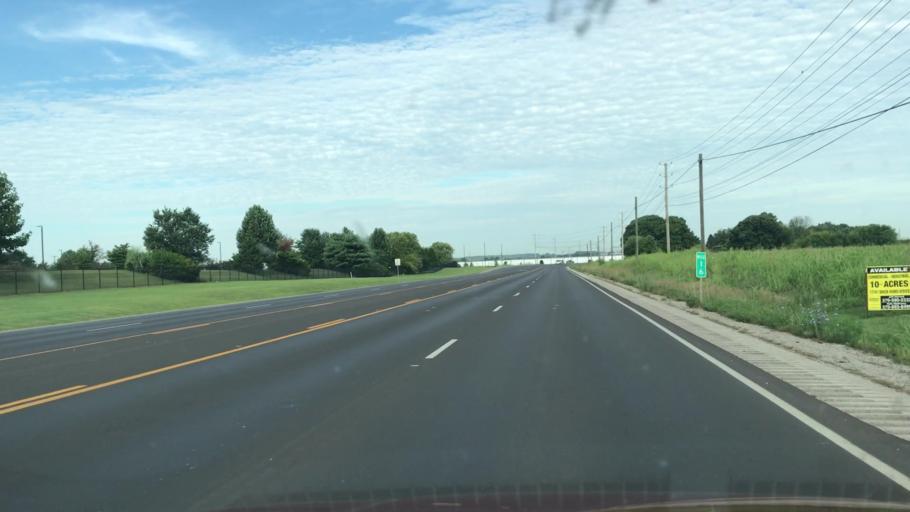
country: US
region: Kentucky
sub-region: Warren County
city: Bowling Green
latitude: 37.0332
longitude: -86.3226
